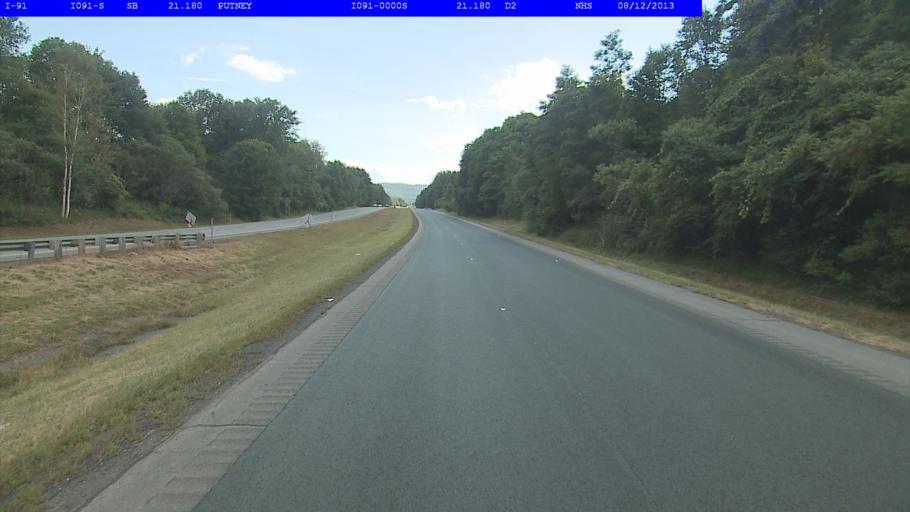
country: US
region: New Hampshire
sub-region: Cheshire County
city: Westmoreland
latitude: 42.9891
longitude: -72.4790
